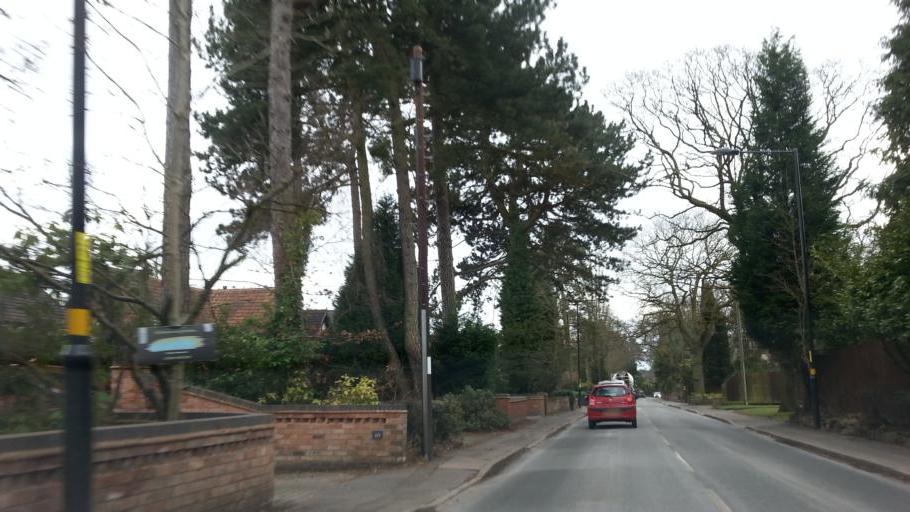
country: GB
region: England
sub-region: Walsall
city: Streetly
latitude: 52.5922
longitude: -1.8628
